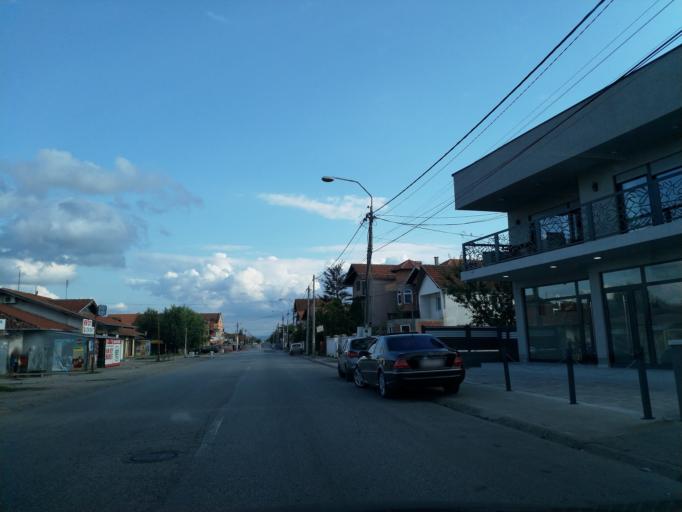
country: RS
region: Central Serbia
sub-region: Pomoravski Okrug
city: Paracin
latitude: 43.8521
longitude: 21.4131
